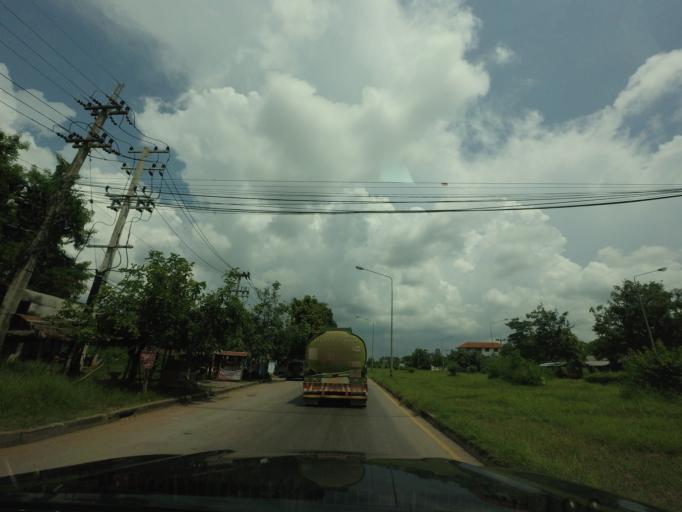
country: TH
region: Khon Kaen
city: Nong Ruea
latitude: 16.4891
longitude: 102.4057
